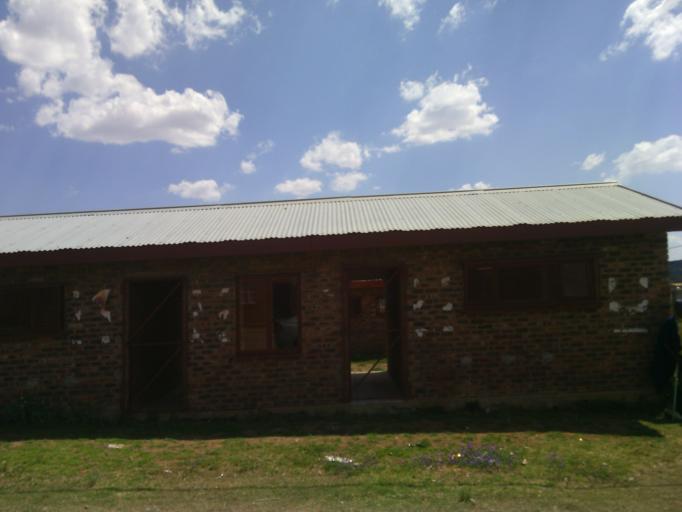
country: ZA
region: Orange Free State
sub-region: Xhariep District Municipality
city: Dewetsdorp
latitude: -29.5811
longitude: 26.6790
